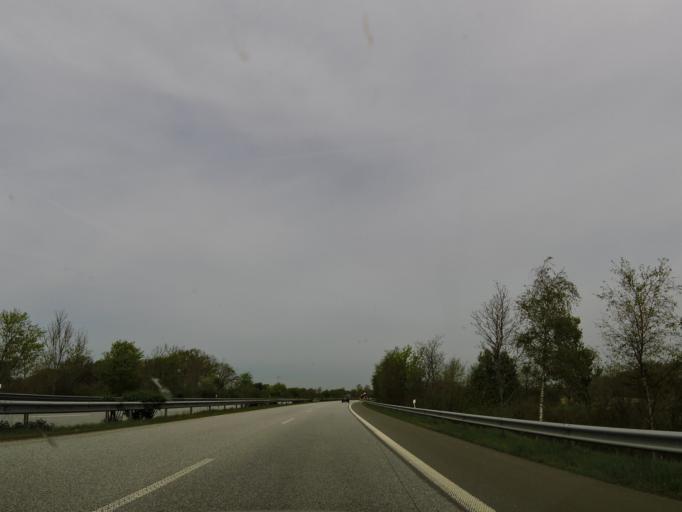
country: DE
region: Schleswig-Holstein
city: Schafstedt
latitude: 54.0793
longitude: 9.2733
